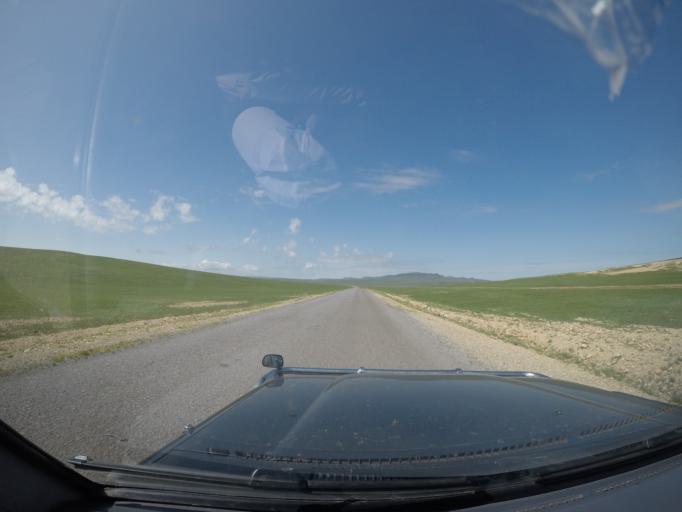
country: MN
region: Hentiy
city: Dundburd
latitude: 47.3451
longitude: 111.5107
